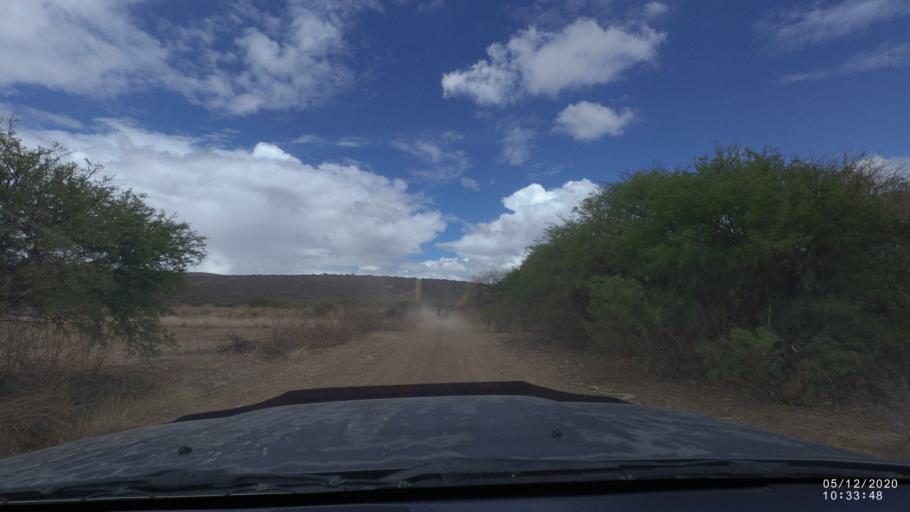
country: BO
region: Cochabamba
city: Sipe Sipe
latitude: -17.5458
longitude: -66.2747
